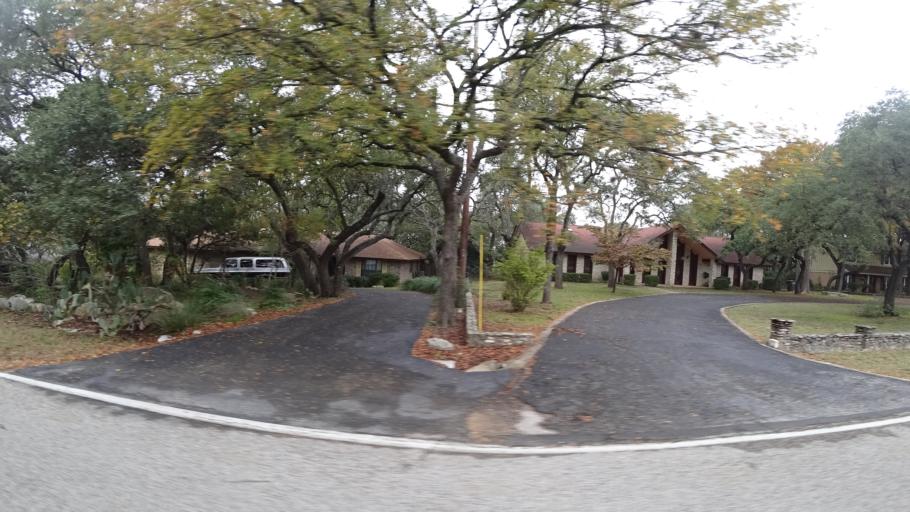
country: US
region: Texas
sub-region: Travis County
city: Shady Hollow
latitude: 30.2230
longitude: -97.8979
